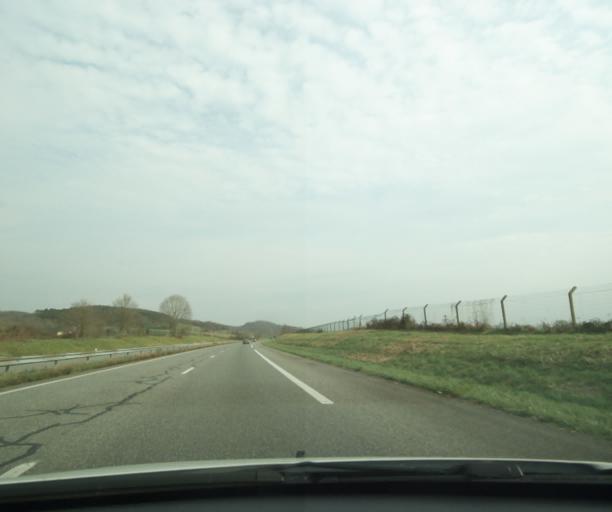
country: FR
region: Aquitaine
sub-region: Departement des Pyrenees-Atlantiques
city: Denguin
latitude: 43.3844
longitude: -0.5115
